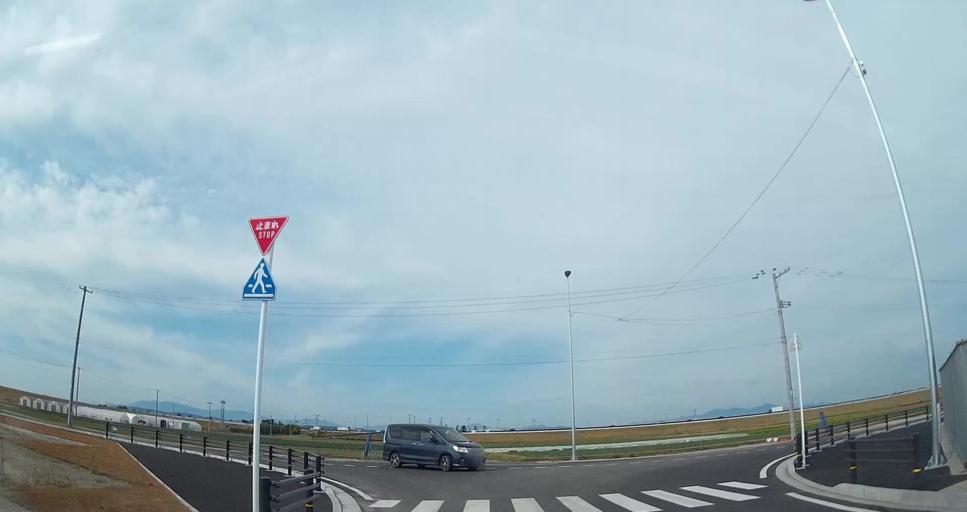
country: JP
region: Miyagi
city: Sendai
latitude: 38.1849
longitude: 140.9545
